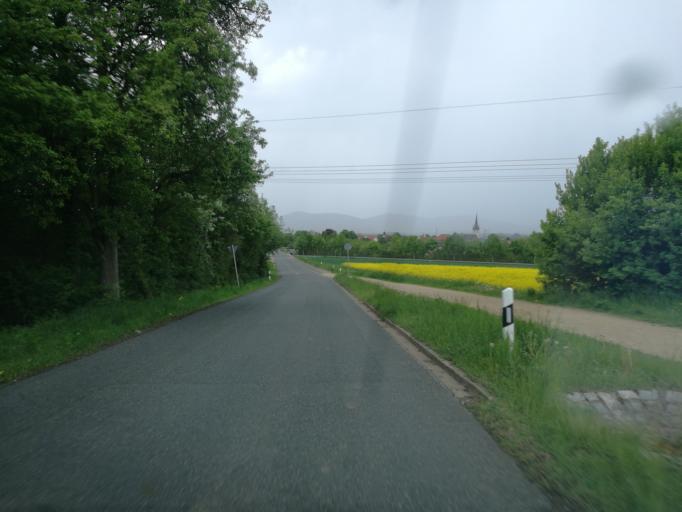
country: DE
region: Bavaria
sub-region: Upper Franconia
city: Bad Staffelstein
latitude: 50.0997
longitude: 11.0120
